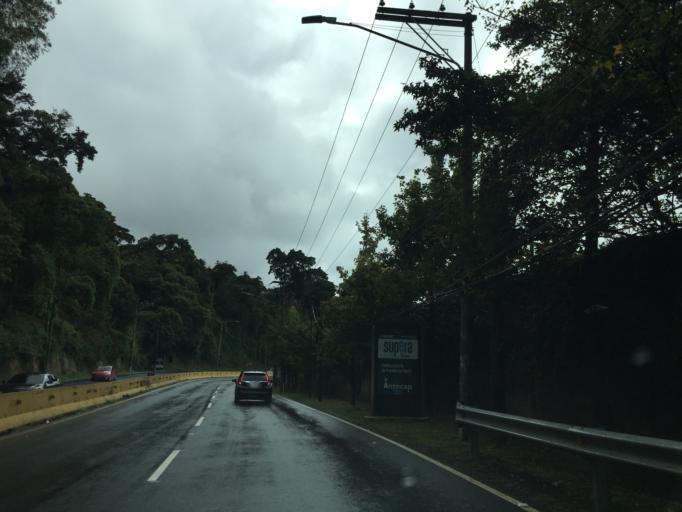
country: GT
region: Guatemala
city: Santa Catarina Pinula
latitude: 14.5785
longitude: -90.4889
